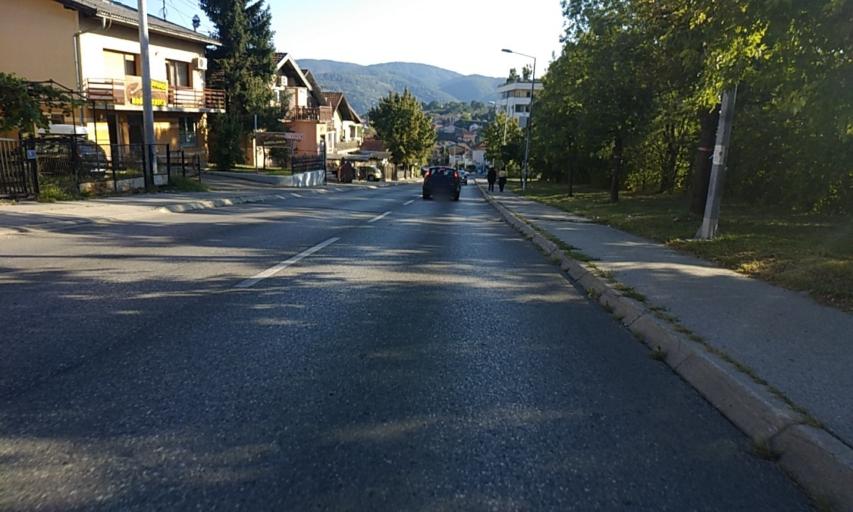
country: BA
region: Republika Srpska
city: Banja Luka
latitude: 44.7779
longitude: 17.1783
